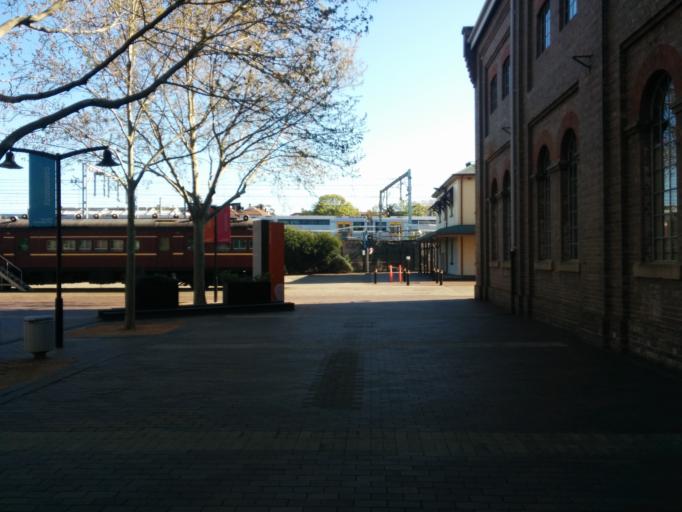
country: AU
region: New South Wales
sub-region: City of Sydney
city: Darlington
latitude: -33.8940
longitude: 151.1969
